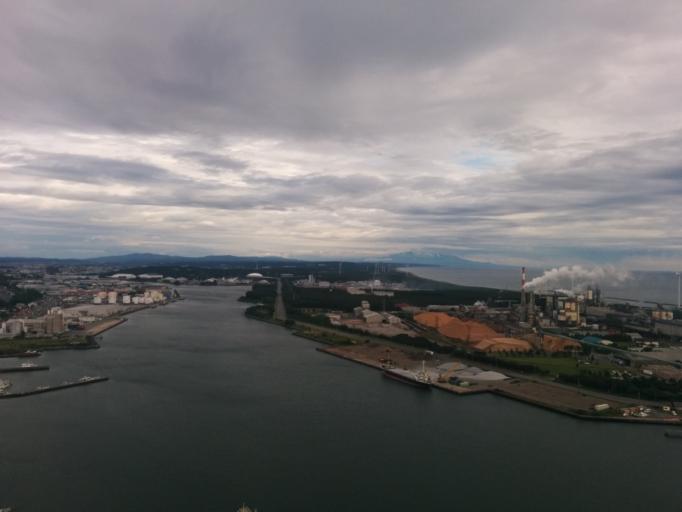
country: JP
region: Akita
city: Akita Shi
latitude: 39.7528
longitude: 140.0615
